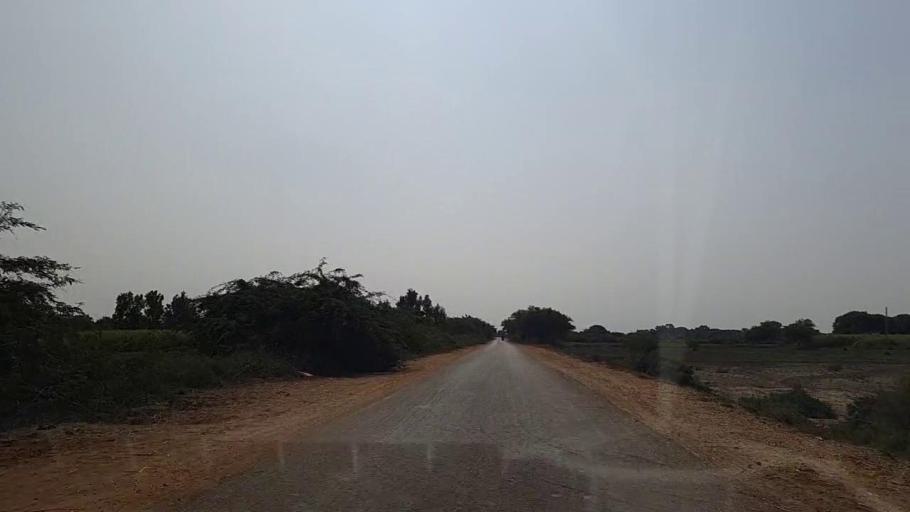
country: PK
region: Sindh
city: Chuhar Jamali
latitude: 24.2516
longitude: 67.9059
